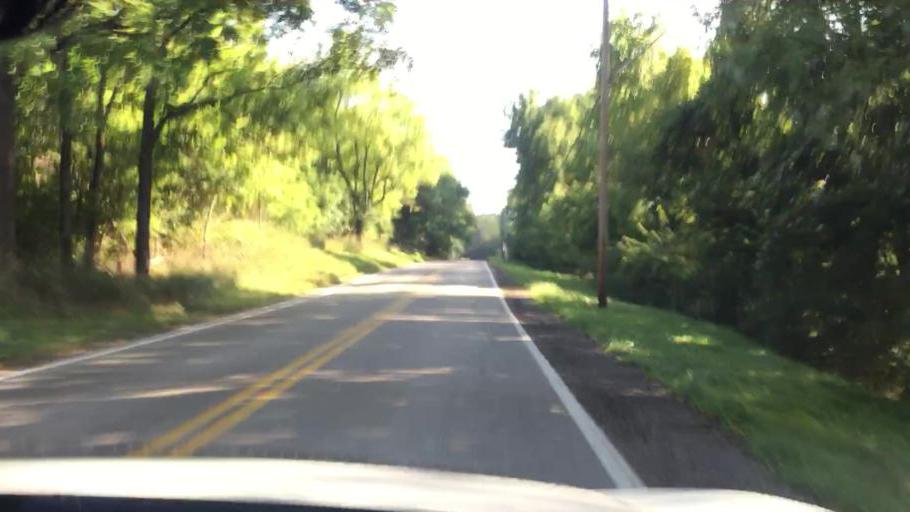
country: US
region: Ohio
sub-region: Clark County
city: Northridge
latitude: 39.9852
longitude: -83.7055
